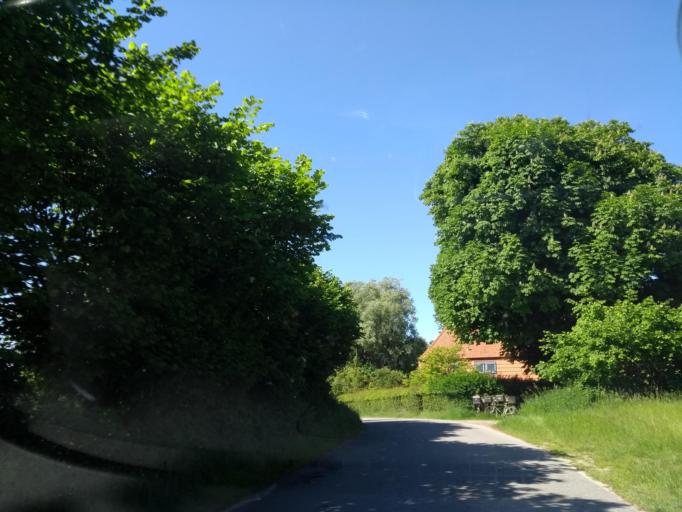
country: DE
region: Schleswig-Holstein
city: Waabs
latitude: 54.5512
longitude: 9.9820
